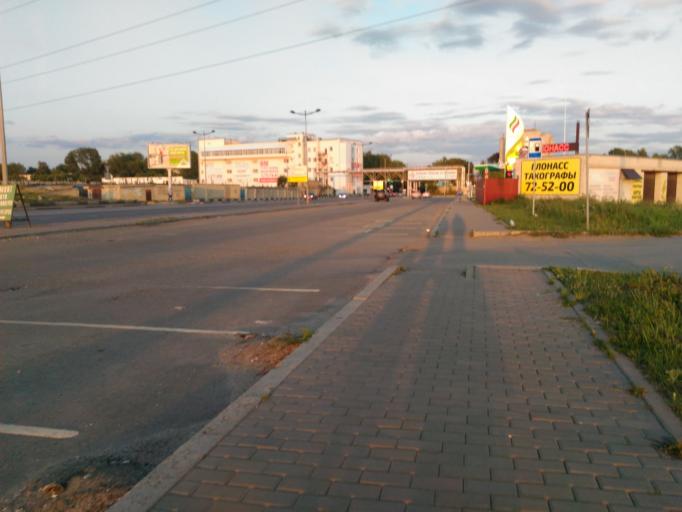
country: RU
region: Ulyanovsk
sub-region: Ulyanovskiy Rayon
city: Ulyanovsk
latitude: 54.2861
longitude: 48.2812
